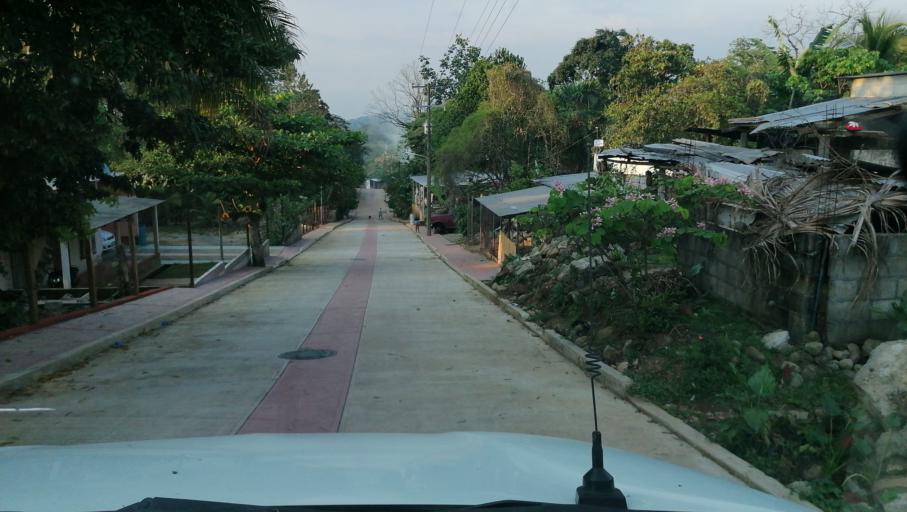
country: MX
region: Chiapas
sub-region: Juarez
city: El Triunfo 1ra. Seccion (Cardona)
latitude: 17.4919
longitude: -93.2433
